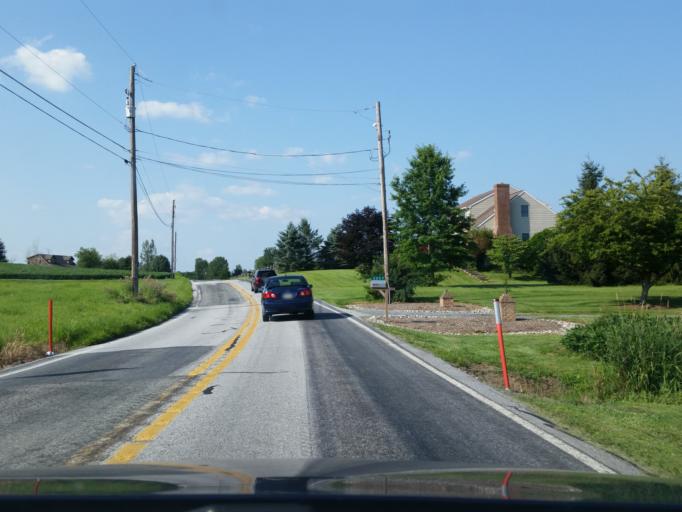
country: US
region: Pennsylvania
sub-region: Lancaster County
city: Mount Joy
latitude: 40.1739
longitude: -76.4967
